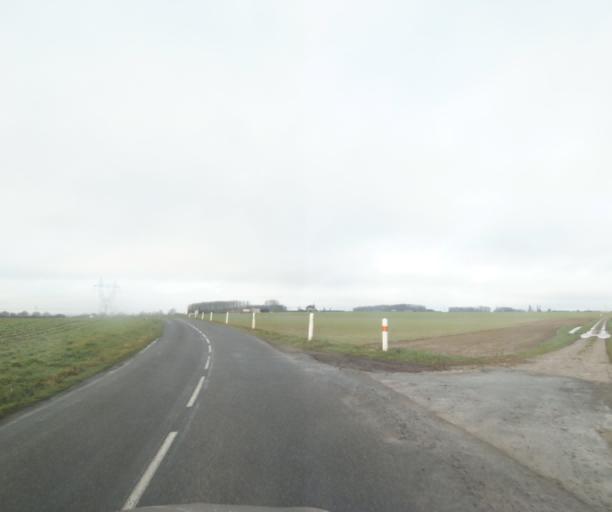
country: FR
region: Nord-Pas-de-Calais
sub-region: Departement du Nord
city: Artres
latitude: 50.2994
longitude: 3.5249
